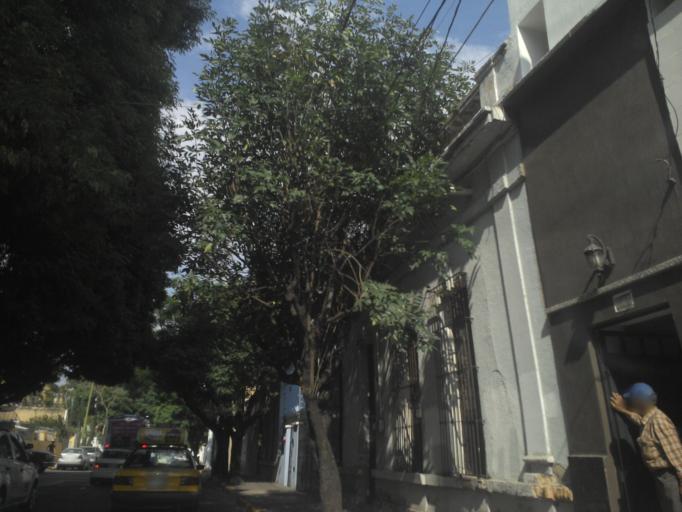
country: MX
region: Jalisco
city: Guadalajara
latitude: 20.6739
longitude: -103.3618
